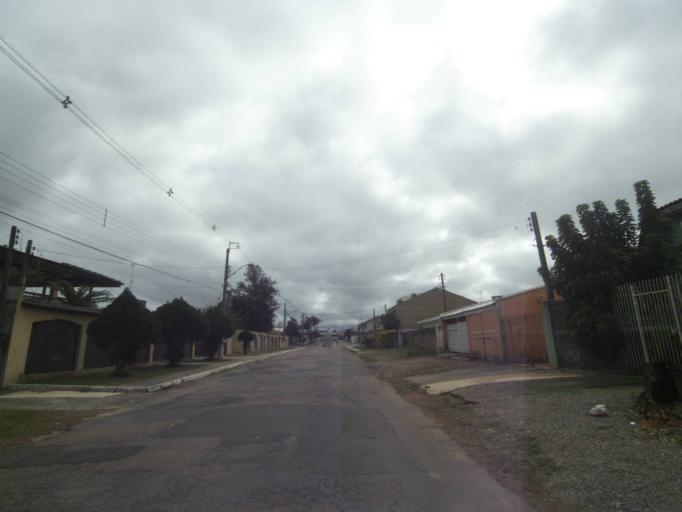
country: BR
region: Parana
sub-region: Sao Jose Dos Pinhais
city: Sao Jose dos Pinhais
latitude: -25.5379
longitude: -49.2967
